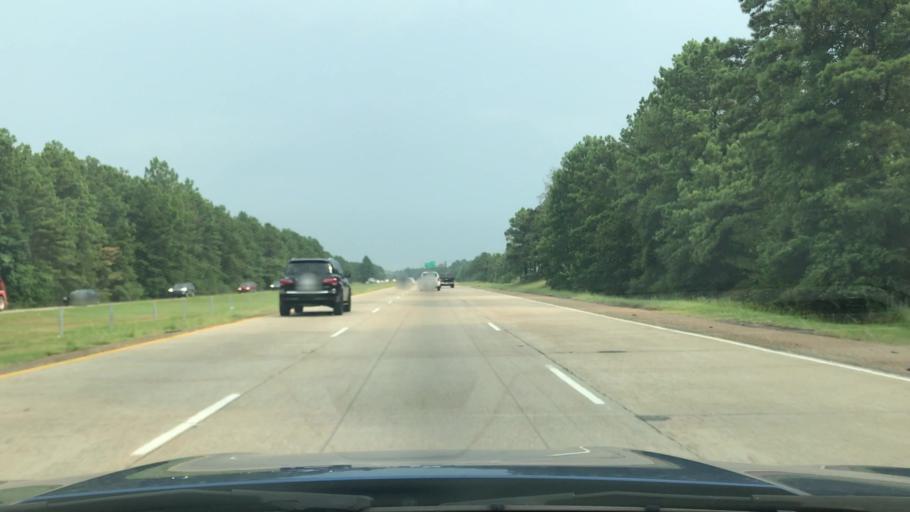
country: US
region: Louisiana
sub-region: Caddo Parish
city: Shreveport
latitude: 32.4379
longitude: -93.8414
